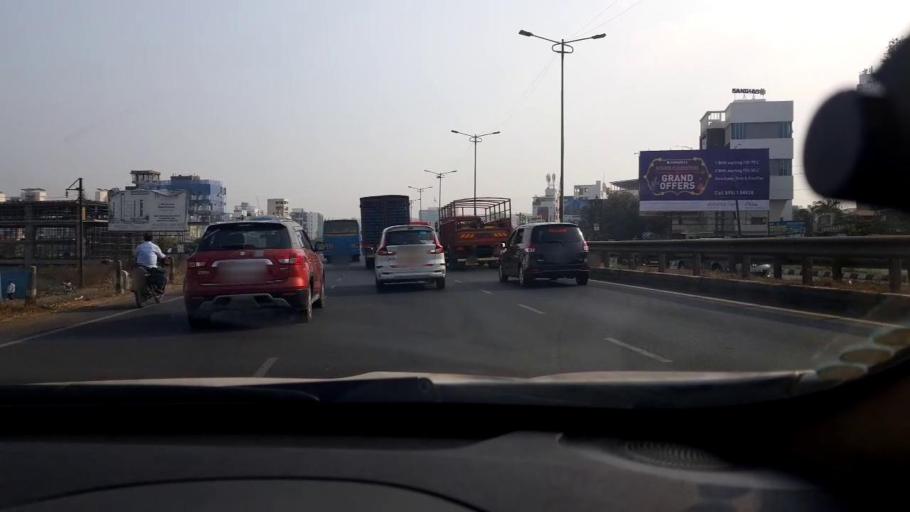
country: IN
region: Maharashtra
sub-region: Pune Division
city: Pimpri
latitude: 18.5658
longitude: 73.7672
